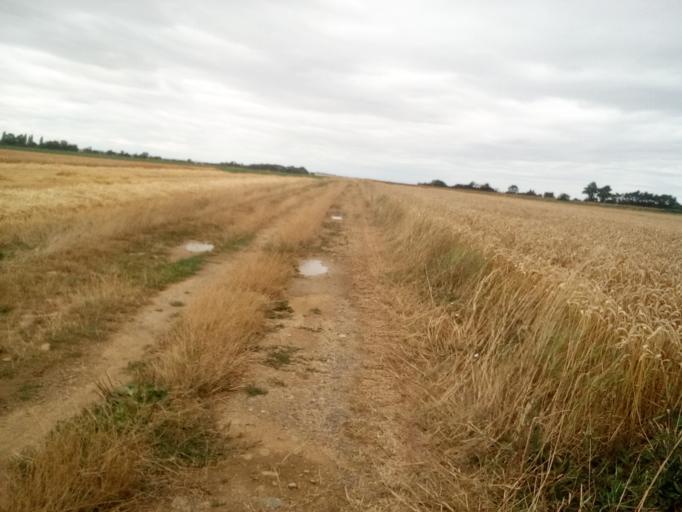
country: FR
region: Lower Normandy
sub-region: Departement du Calvados
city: Clinchamps-sur-Orne
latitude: 49.0566
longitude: -0.4112
